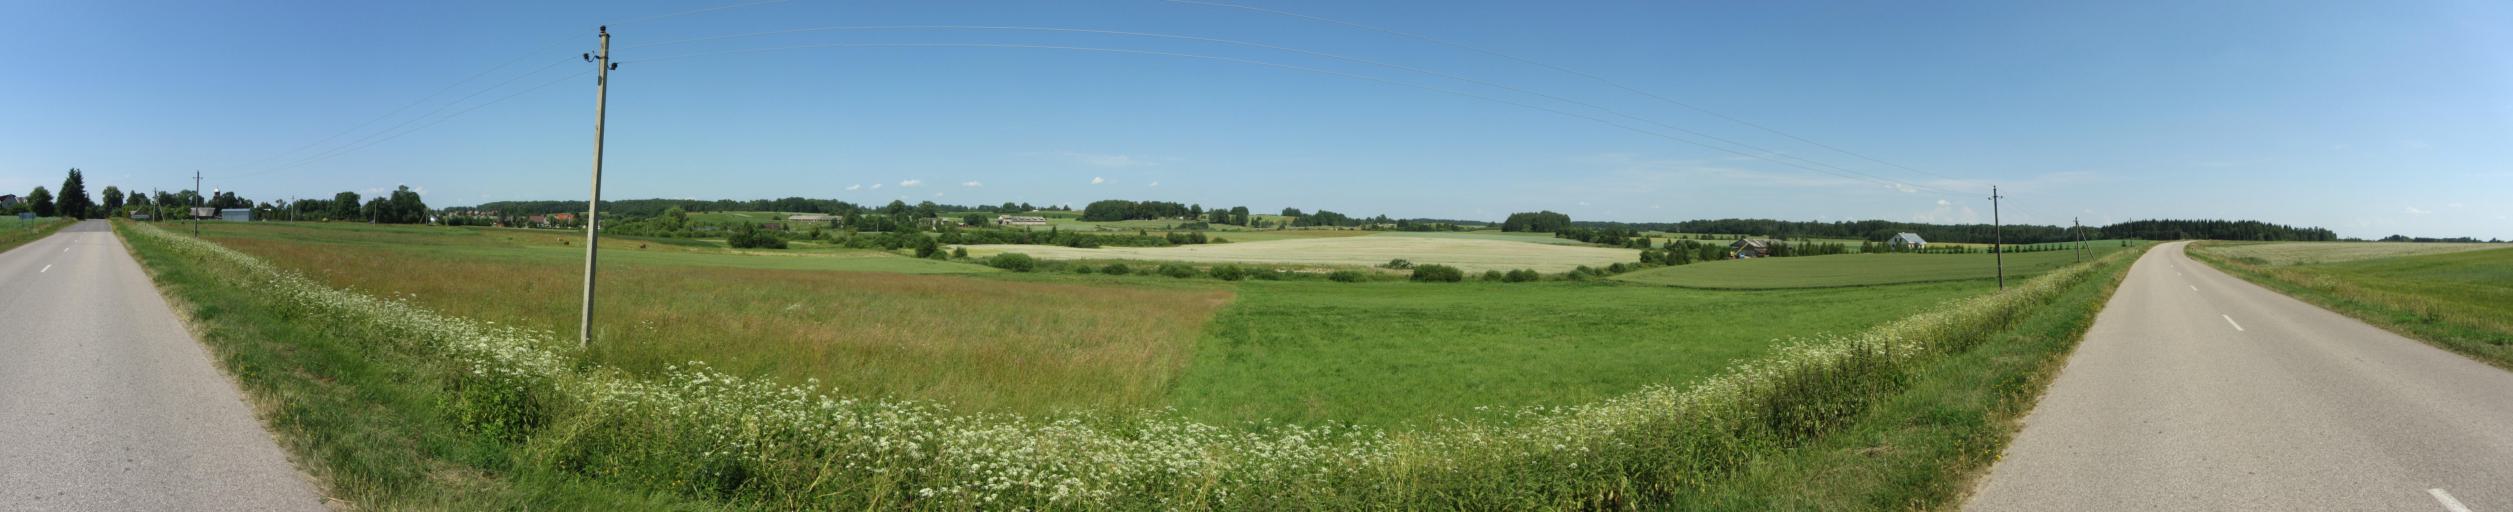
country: LT
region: Vilnius County
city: Ukmerge
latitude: 55.3009
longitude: 24.9819
